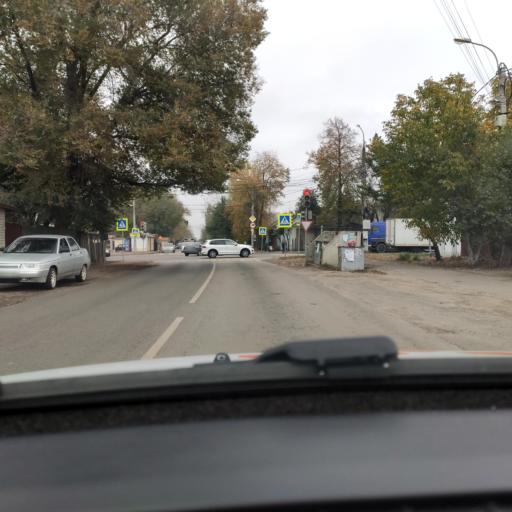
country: RU
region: Voronezj
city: Voronezh
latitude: 51.6336
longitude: 39.1896
